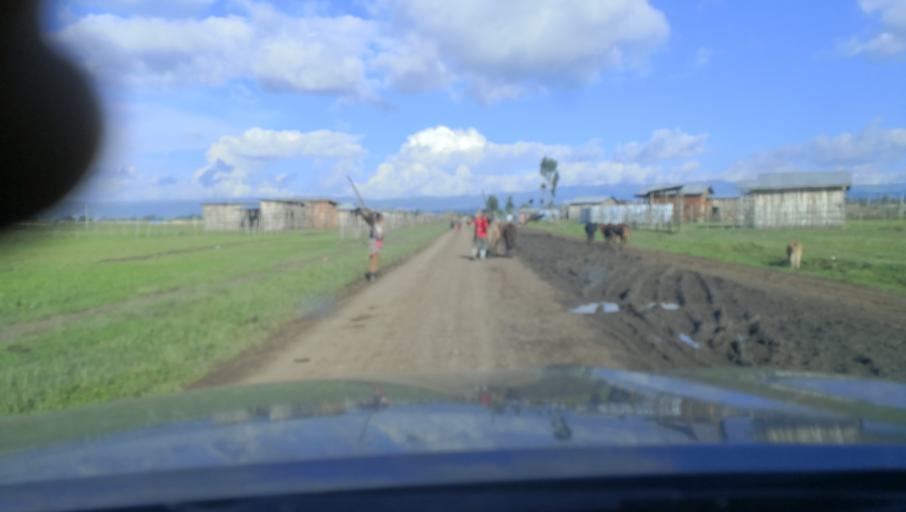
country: ET
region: Oromiya
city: Tulu Bolo
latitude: 8.4754
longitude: 38.2415
